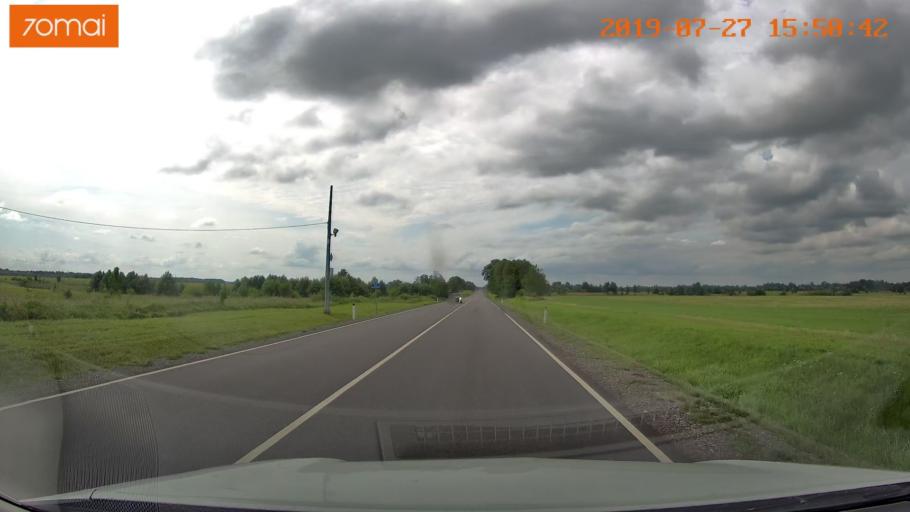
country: RU
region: Kaliningrad
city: Chernyakhovsk
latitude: 54.6015
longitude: 22.0000
